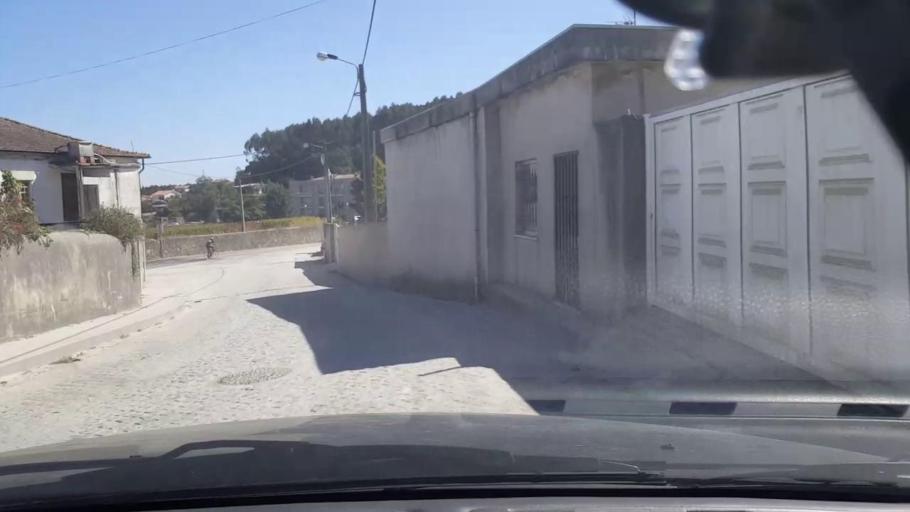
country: PT
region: Porto
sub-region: Maia
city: Gemunde
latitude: 41.3384
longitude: -8.6459
